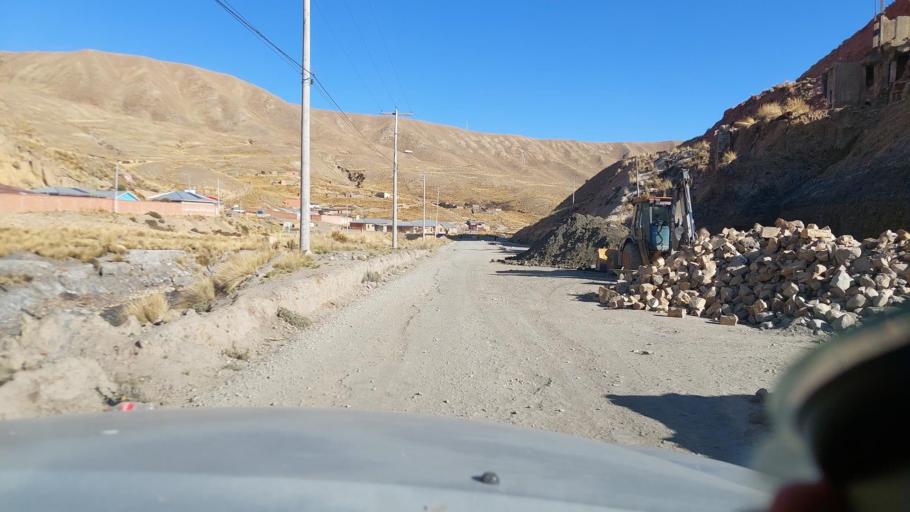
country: BO
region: La Paz
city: La Paz
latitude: -16.4018
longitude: -68.1024
